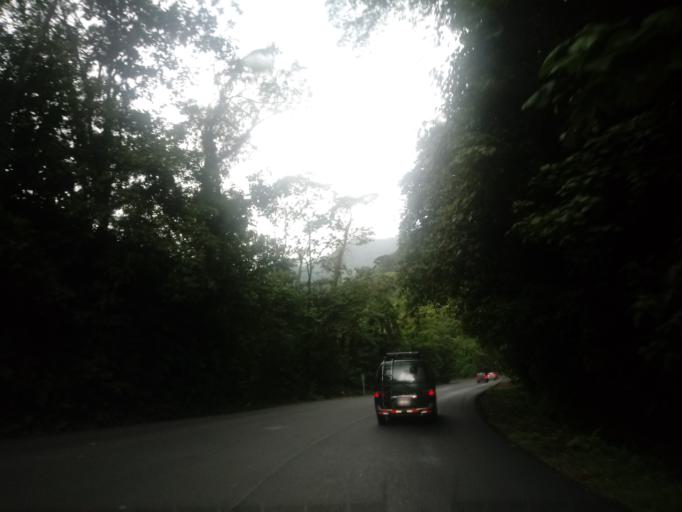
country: CR
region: San Jose
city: Dulce Nombre de Jesus
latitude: 10.1526
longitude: -83.9541
